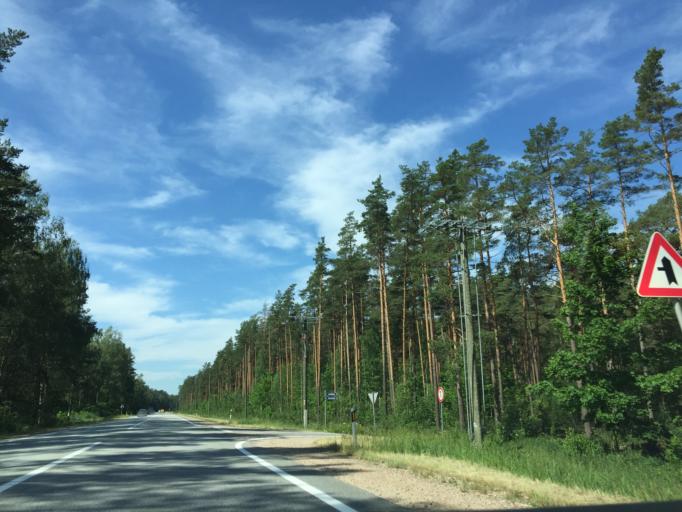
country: LV
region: Jurmala
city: Jurmala
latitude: 56.9358
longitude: 23.7236
